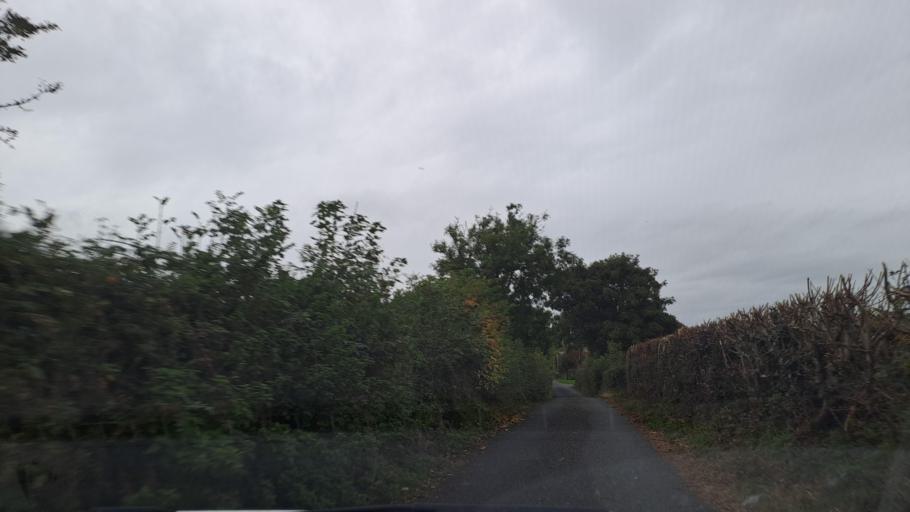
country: IE
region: Ulster
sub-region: County Monaghan
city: Carrickmacross
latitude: 53.9812
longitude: -6.7459
